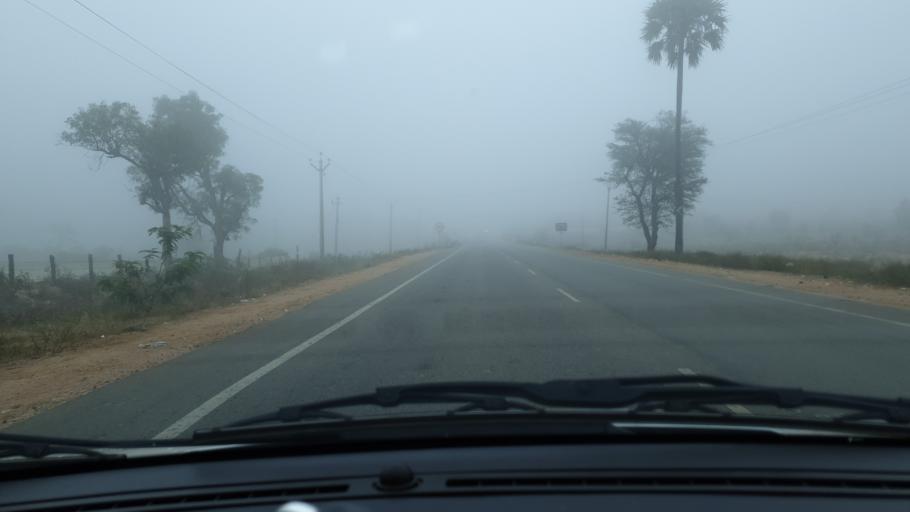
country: IN
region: Telangana
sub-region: Mahbubnagar
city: Nagar Karnul
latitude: 16.6624
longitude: 78.5727
